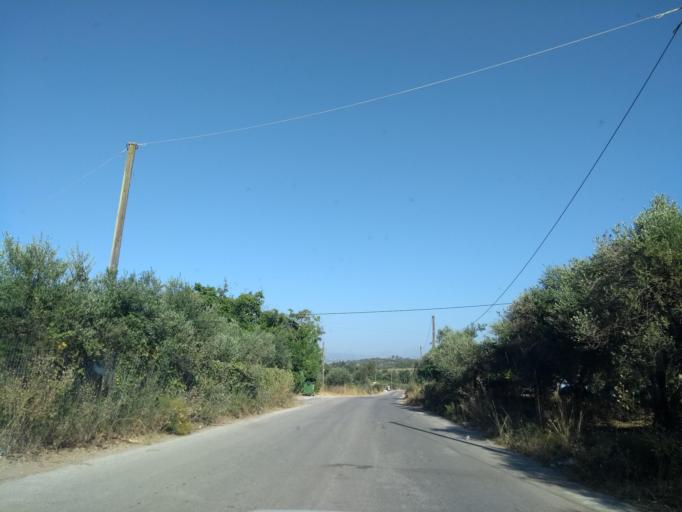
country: GR
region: Crete
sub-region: Nomos Chanias
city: Georgioupolis
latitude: 35.3678
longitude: 24.2317
